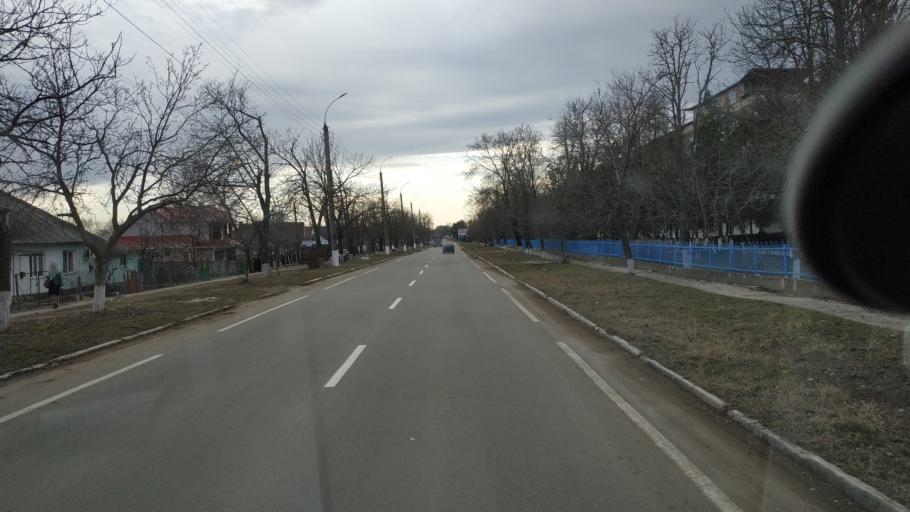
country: MD
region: Criuleni
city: Criuleni
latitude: 47.2066
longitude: 29.1581
